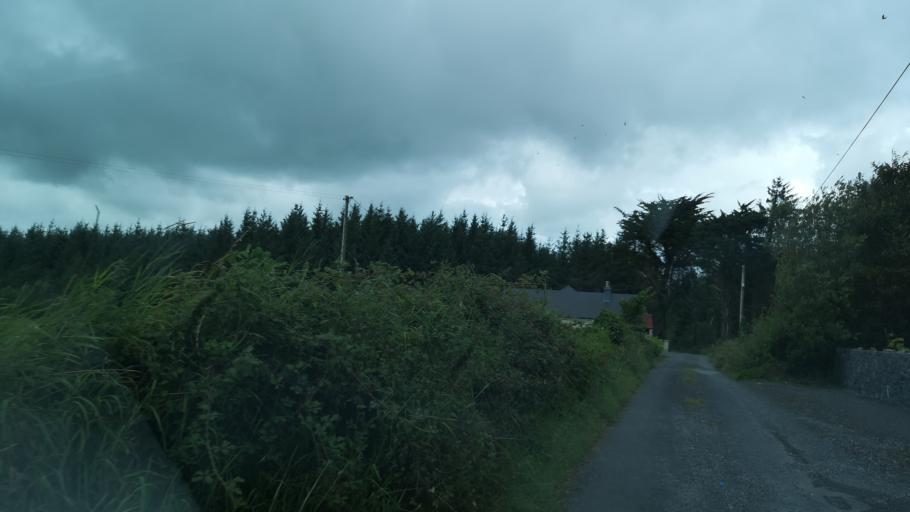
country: IE
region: Connaught
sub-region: County Galway
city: Athenry
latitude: 53.3067
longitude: -8.6986
